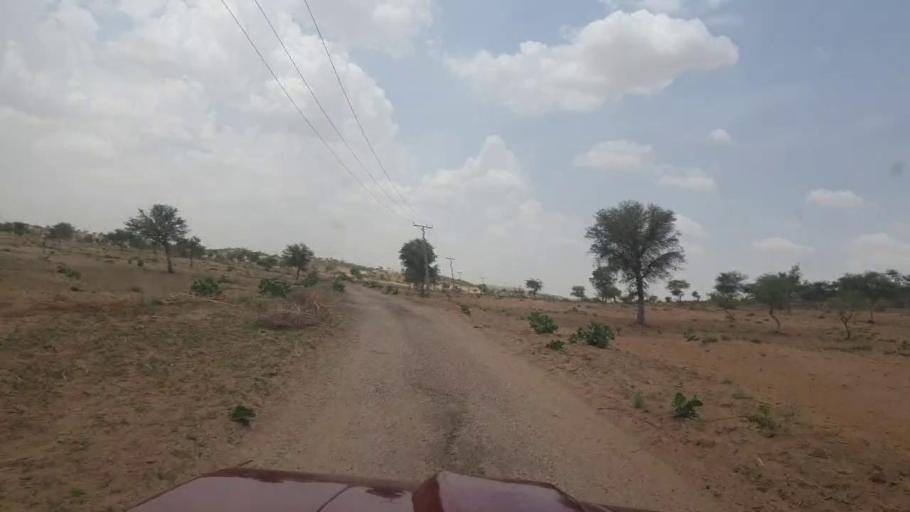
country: PK
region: Sindh
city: Islamkot
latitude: 25.2091
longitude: 70.4522
